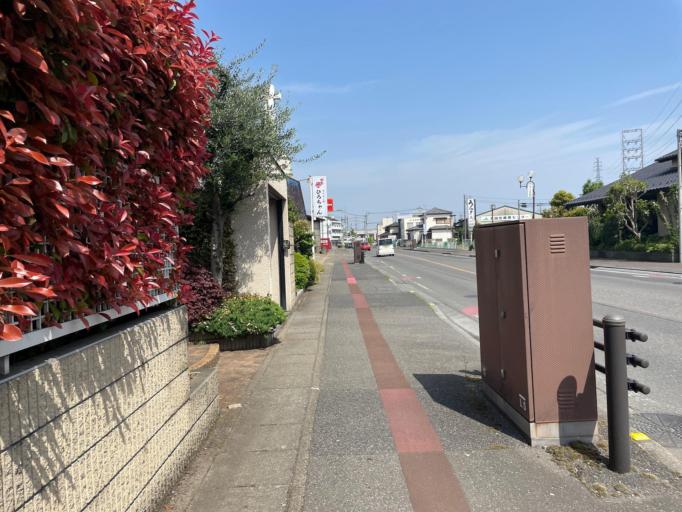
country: JP
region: Gunma
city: Ota
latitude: 36.2961
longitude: 139.3606
